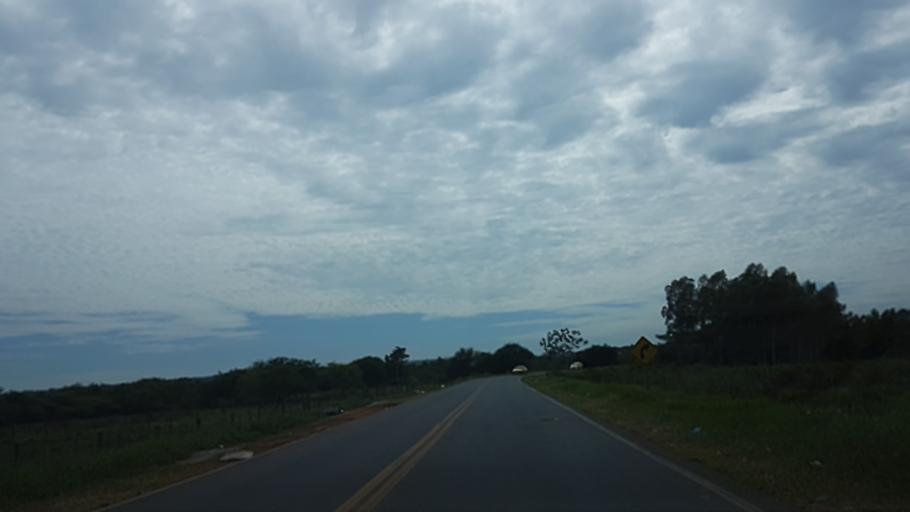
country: PY
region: Central
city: Capiata
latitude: -25.3148
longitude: -57.4580
